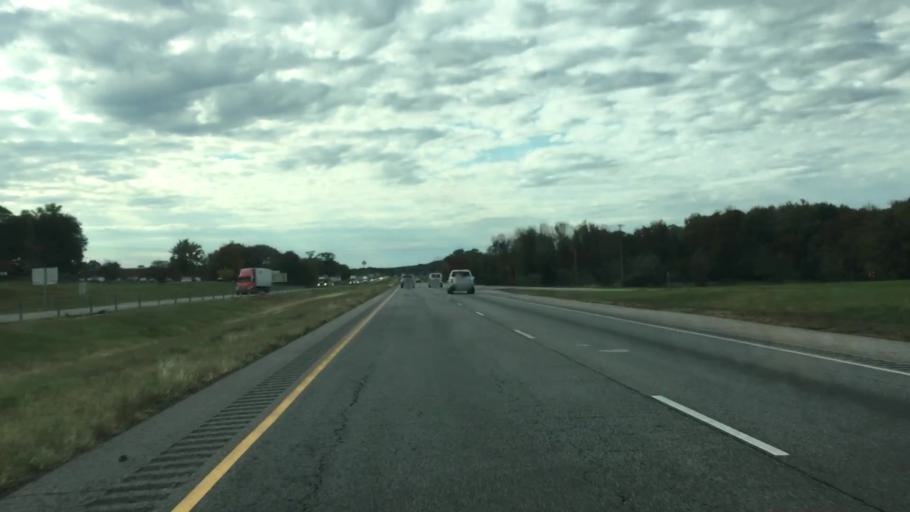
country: US
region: Arkansas
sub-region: Conway County
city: Morrilton
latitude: 35.1743
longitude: -92.7214
